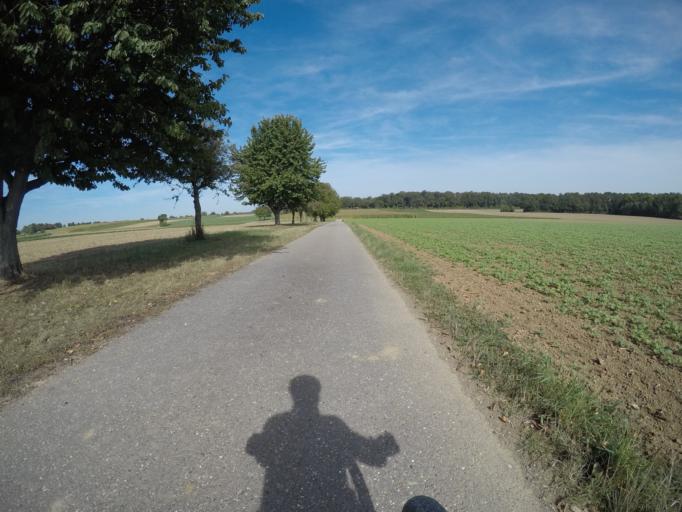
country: DE
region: Baden-Wuerttemberg
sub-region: Regierungsbezirk Stuttgart
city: Oberriexingen
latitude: 48.9457
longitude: 9.0269
